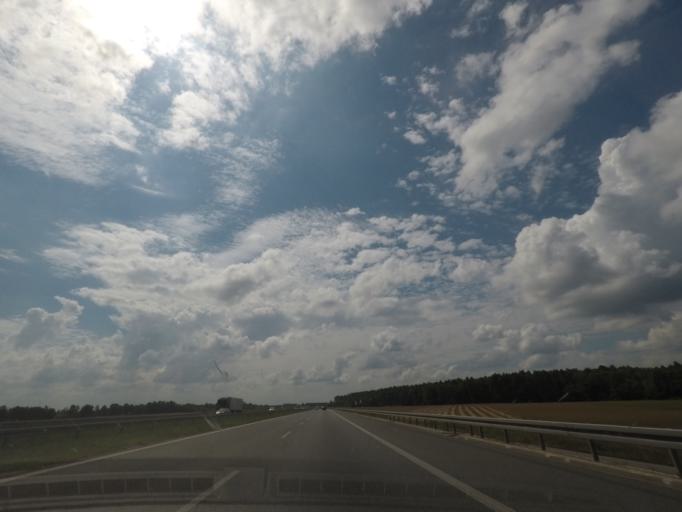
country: PL
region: Lodz Voivodeship
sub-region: Powiat leczycki
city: Piatek
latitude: 52.0265
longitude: 19.5426
